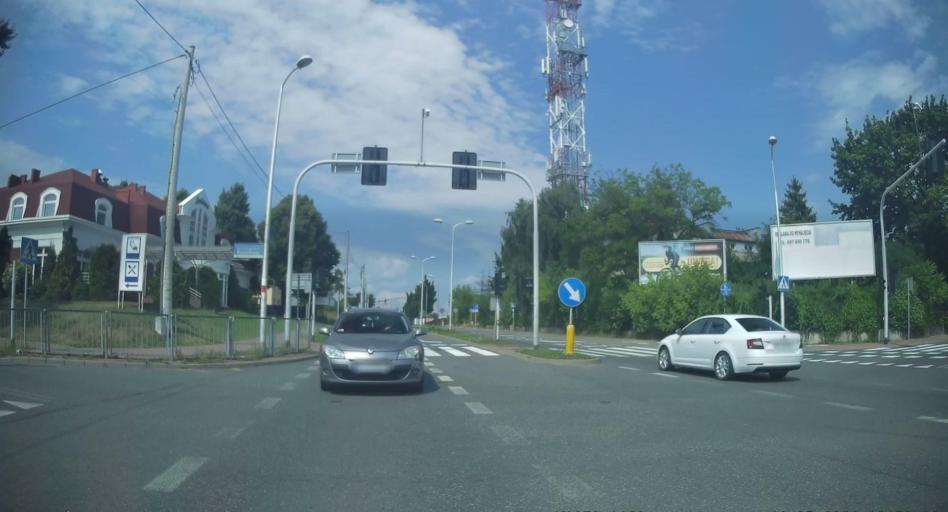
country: PL
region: Silesian Voivodeship
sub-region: Czestochowa
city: Czestochowa
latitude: 50.8141
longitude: 19.0844
